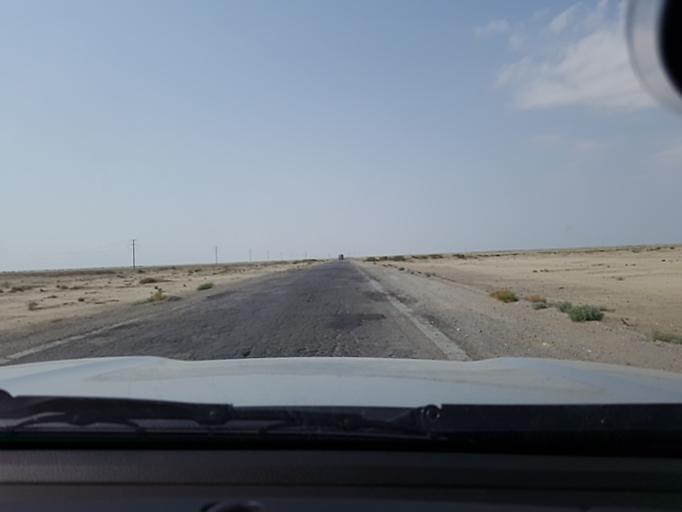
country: TM
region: Balkan
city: Gumdag
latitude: 39.0192
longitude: 54.5849
